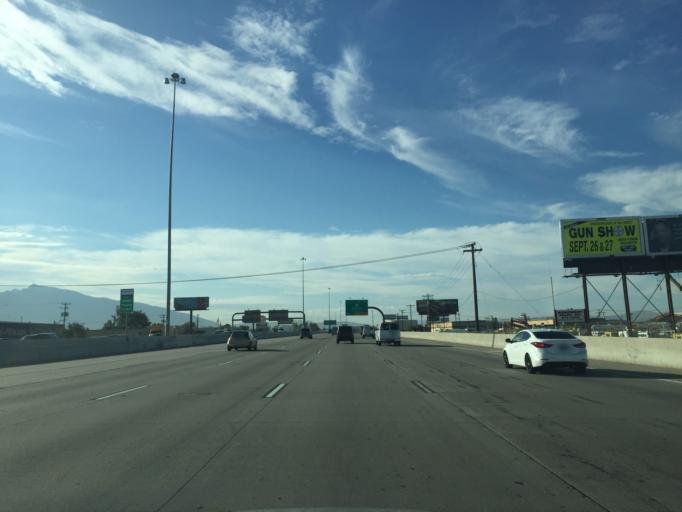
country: US
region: Utah
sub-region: Salt Lake County
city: South Salt Lake
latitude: 40.7114
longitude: -111.9043
